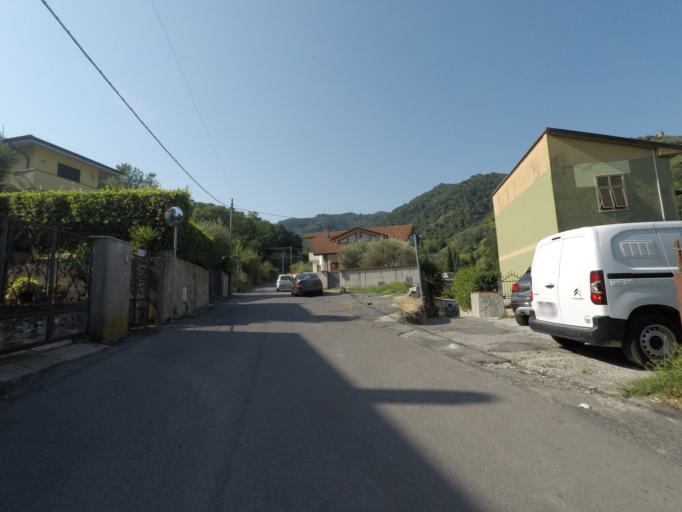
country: IT
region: Tuscany
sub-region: Provincia di Massa-Carrara
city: Carrara
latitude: 44.0742
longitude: 10.0752
